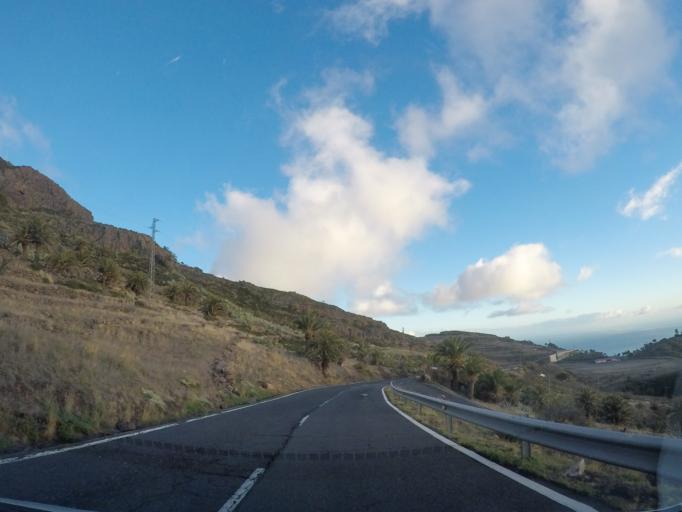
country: ES
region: Canary Islands
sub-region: Provincia de Santa Cruz de Tenerife
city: Alajero
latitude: 28.0754
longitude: -17.2394
